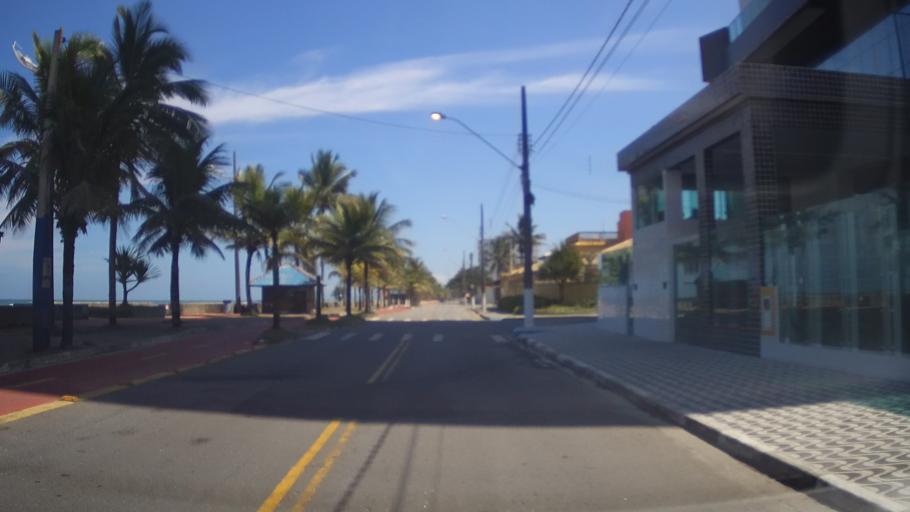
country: BR
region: Sao Paulo
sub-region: Mongagua
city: Mongagua
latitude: -24.1107
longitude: -46.6490
